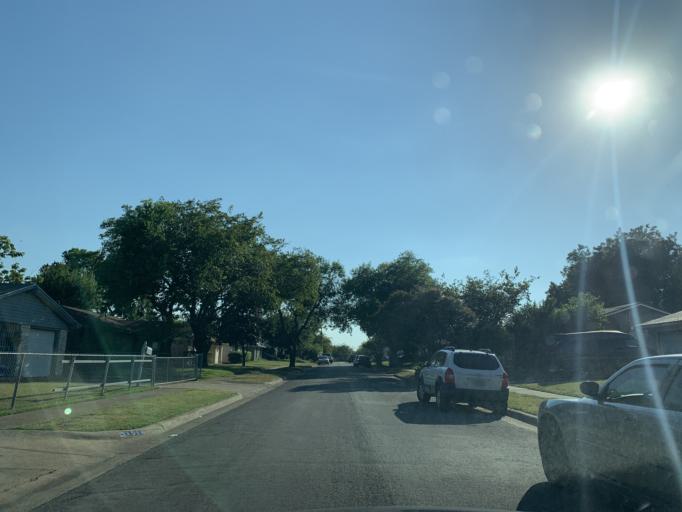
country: US
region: Texas
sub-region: Dallas County
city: Hutchins
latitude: 32.6644
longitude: -96.7630
